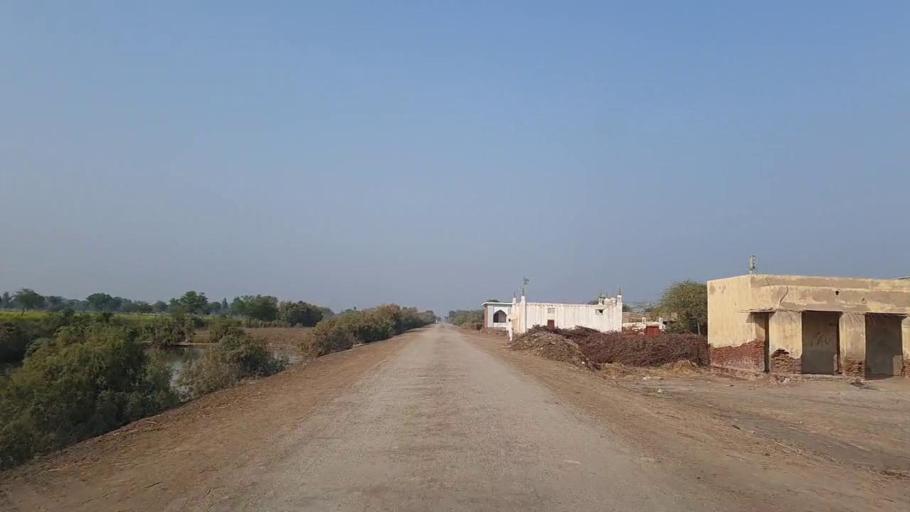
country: PK
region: Sindh
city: Nawabshah
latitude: 26.3377
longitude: 68.4892
